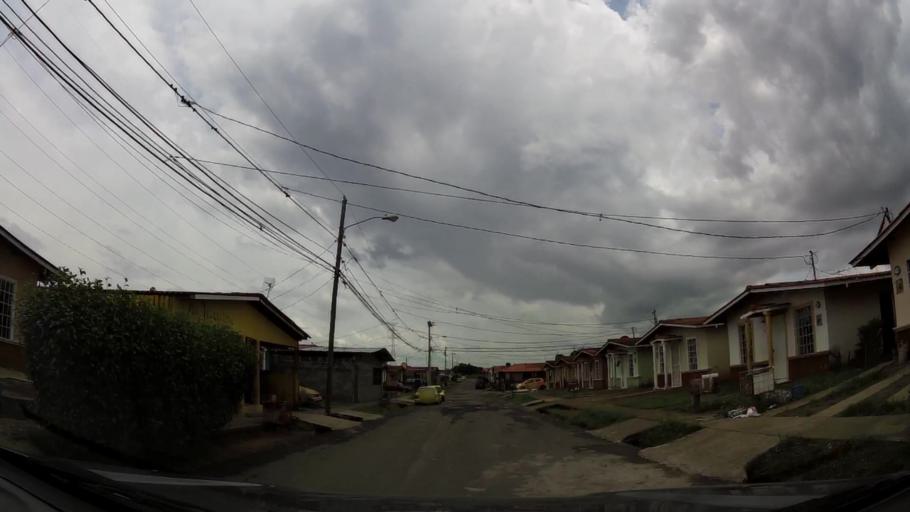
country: PA
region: Panama
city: Cabra Numero Uno
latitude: 9.1130
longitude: -79.3176
